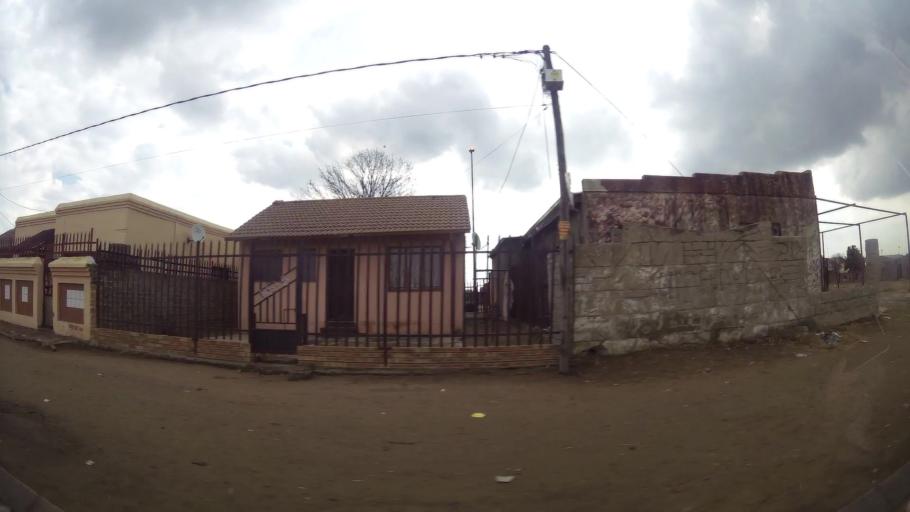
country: ZA
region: Orange Free State
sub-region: Fezile Dabi District Municipality
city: Sasolburg
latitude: -26.8514
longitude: 27.8617
